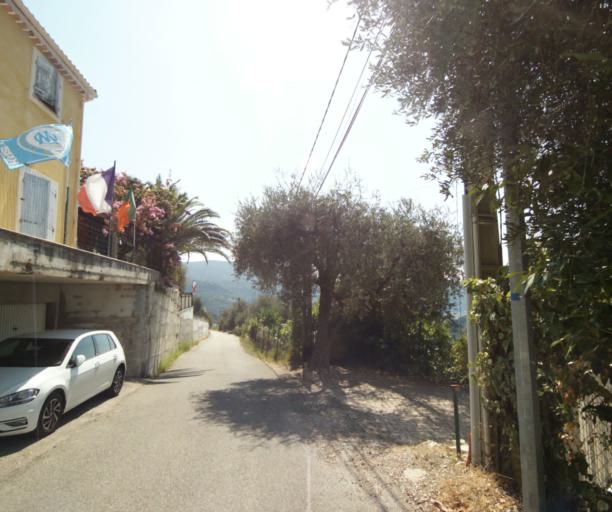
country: FR
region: Provence-Alpes-Cote d'Azur
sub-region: Departement des Alpes-Maritimes
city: Drap
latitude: 43.7597
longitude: 7.3258
